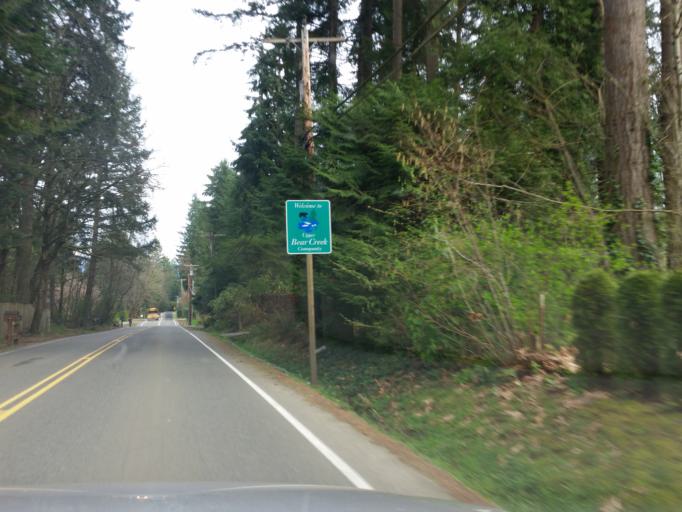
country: US
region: Washington
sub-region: King County
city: Cottage Lake
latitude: 47.7531
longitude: -122.1189
